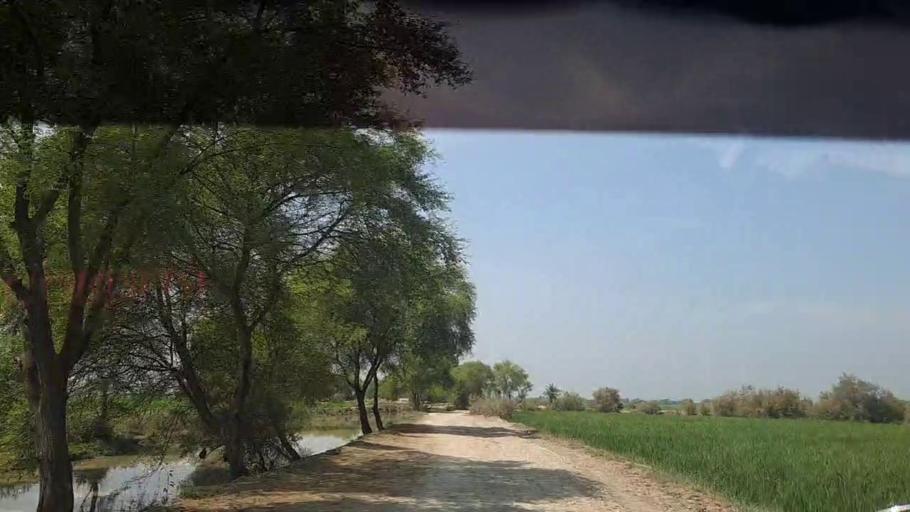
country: PK
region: Sindh
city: Thul
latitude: 28.1908
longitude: 68.7133
